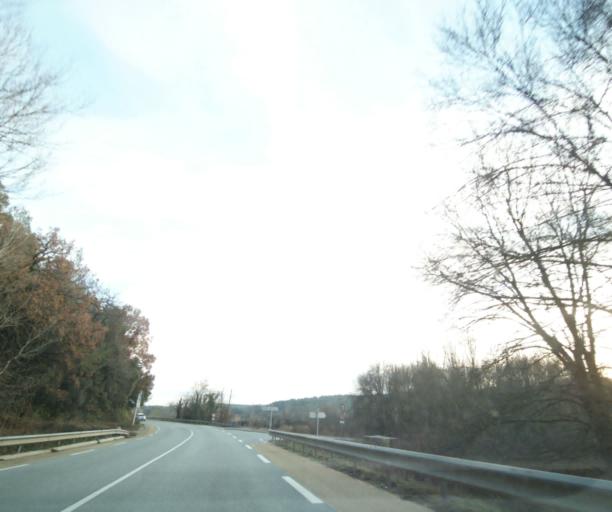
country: FR
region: Provence-Alpes-Cote d'Azur
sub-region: Departement du Var
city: Trans-en-Provence
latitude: 43.4962
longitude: 6.5098
